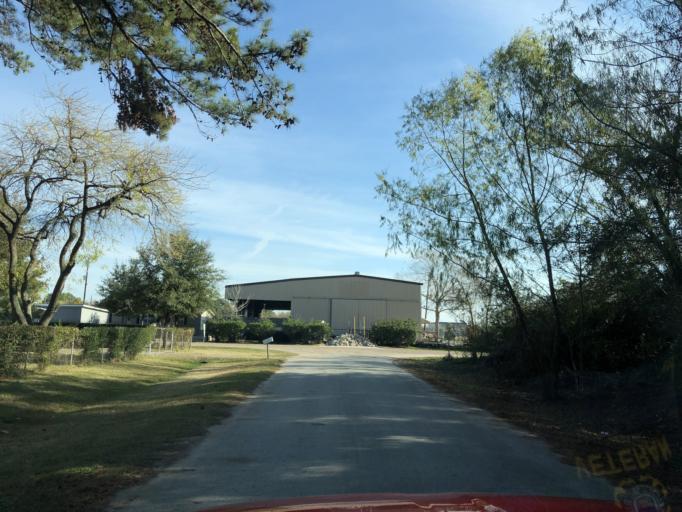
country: US
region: Texas
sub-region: Harris County
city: Tomball
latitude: 30.0440
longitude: -95.5458
